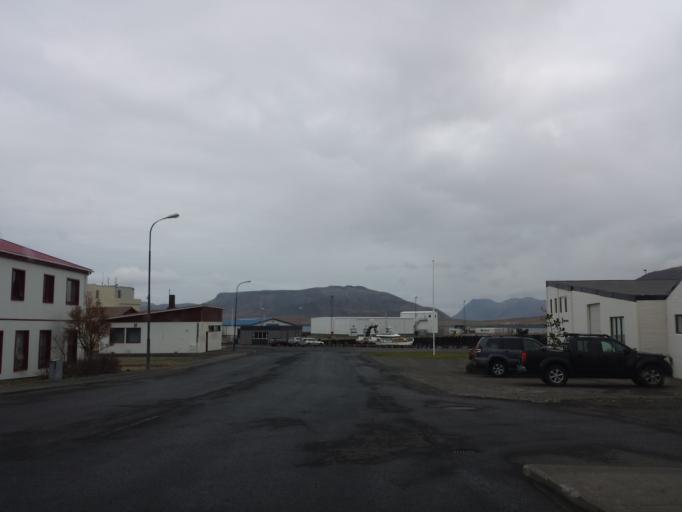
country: IS
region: West
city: Olafsvik
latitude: 64.9247
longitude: -23.2570
